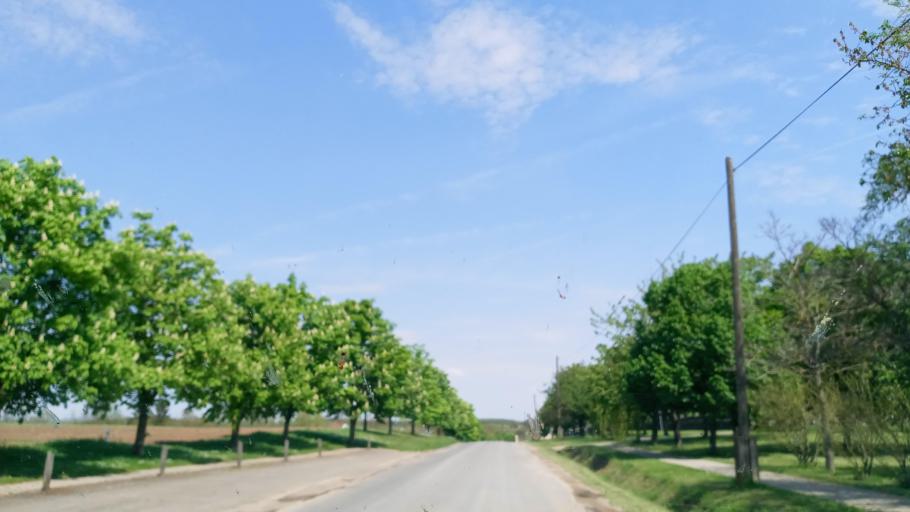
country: HU
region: Baranya
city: Boly
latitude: 45.9181
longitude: 18.5441
